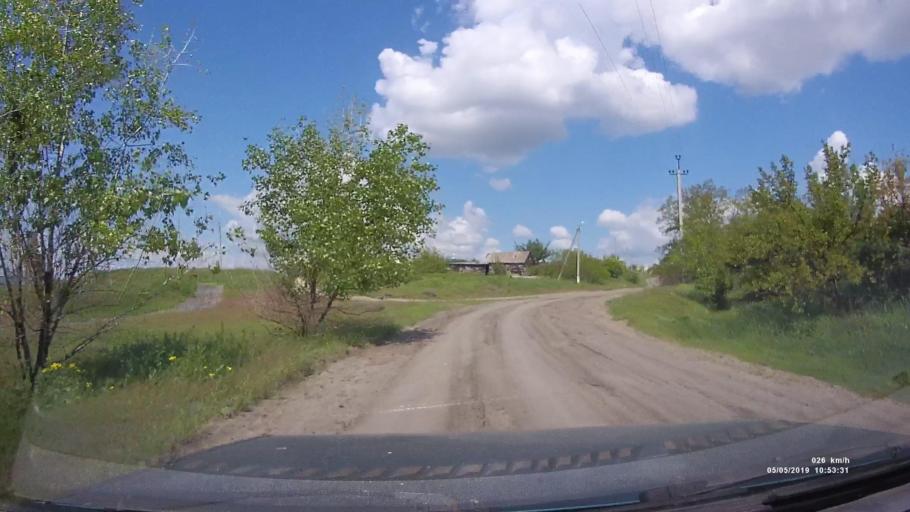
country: RU
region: Rostov
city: Ust'-Donetskiy
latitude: 47.6545
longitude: 40.8246
